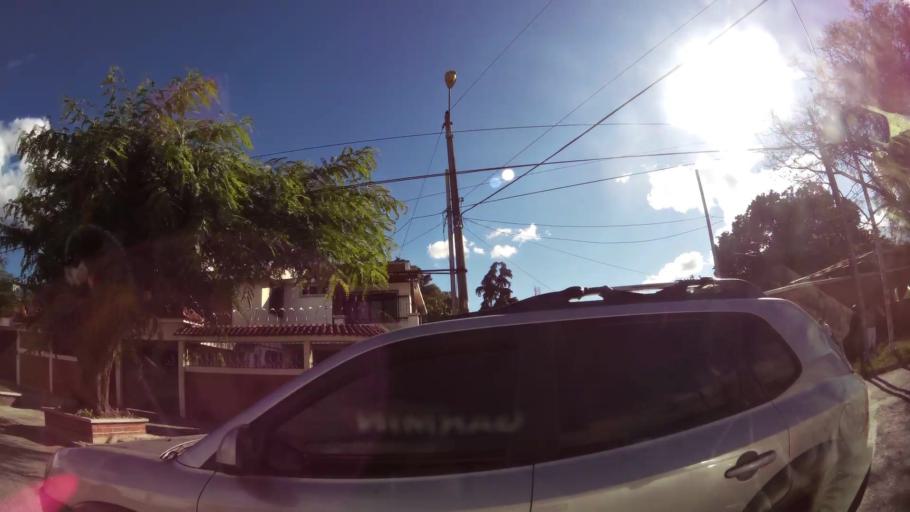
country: GT
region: Guatemala
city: Guatemala City
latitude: 14.6073
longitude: -90.5559
